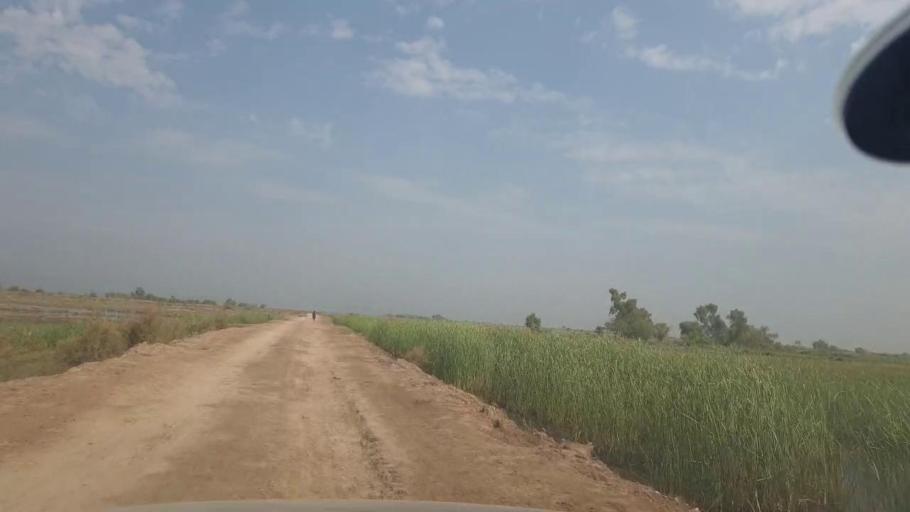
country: PK
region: Balochistan
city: Mehrabpur
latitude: 28.0284
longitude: 68.1321
